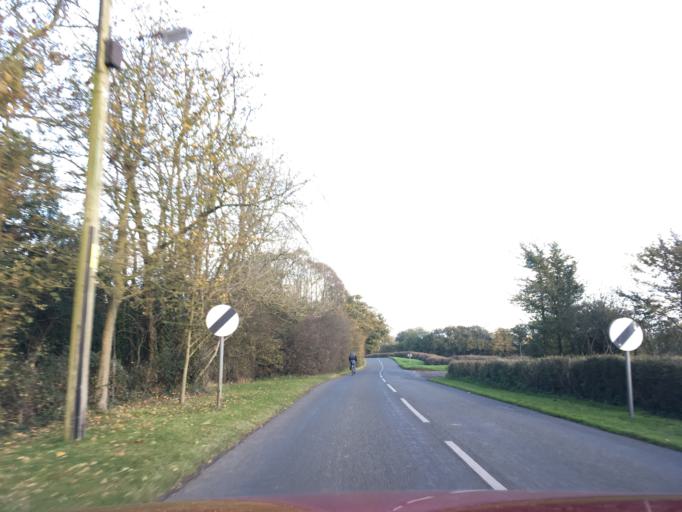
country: GB
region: England
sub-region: Gloucestershire
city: Berkeley
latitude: 51.7105
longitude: -2.4587
